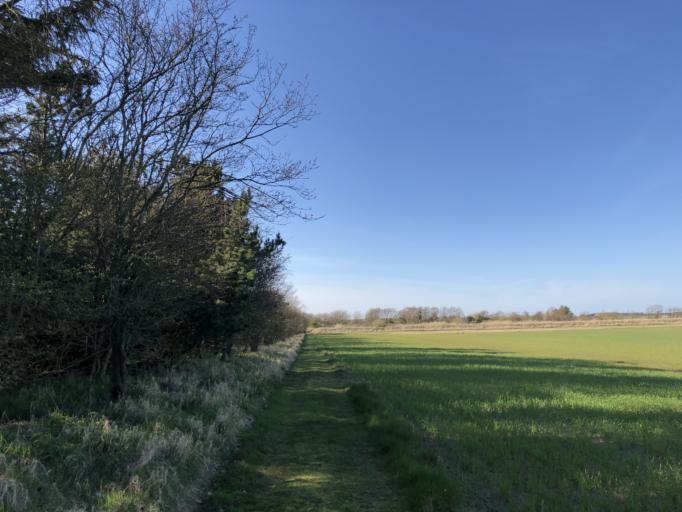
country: DK
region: Central Jutland
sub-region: Holstebro Kommune
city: Ulfborg
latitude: 56.3293
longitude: 8.3148
